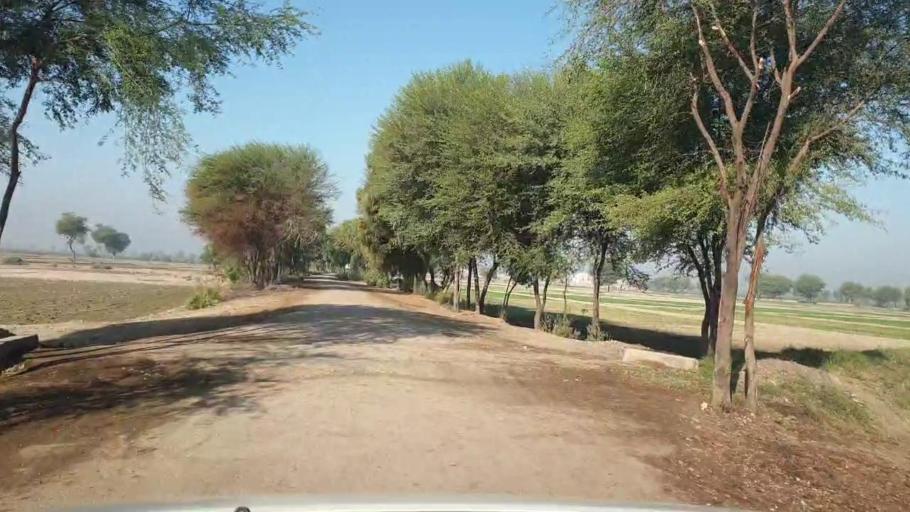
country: PK
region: Sindh
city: Dadu
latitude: 26.6750
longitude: 67.8380
